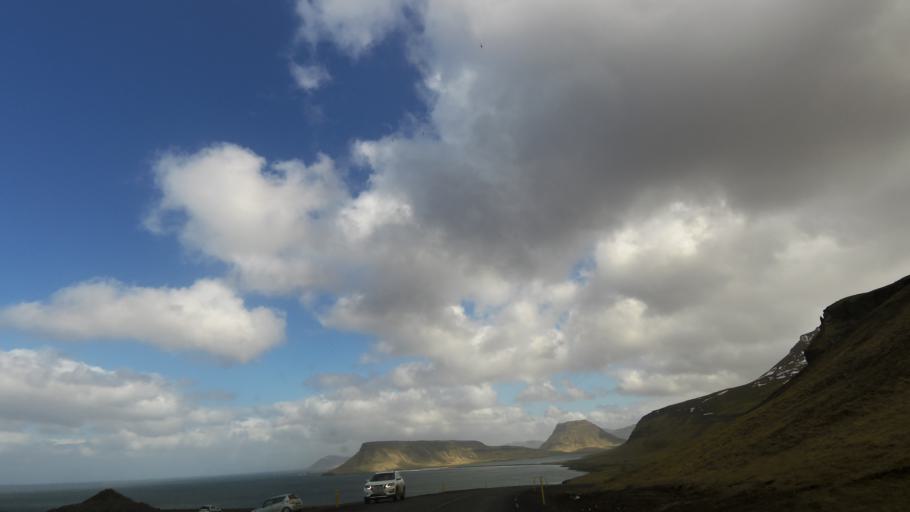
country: IS
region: West
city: Olafsvik
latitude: 64.9496
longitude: -23.4776
